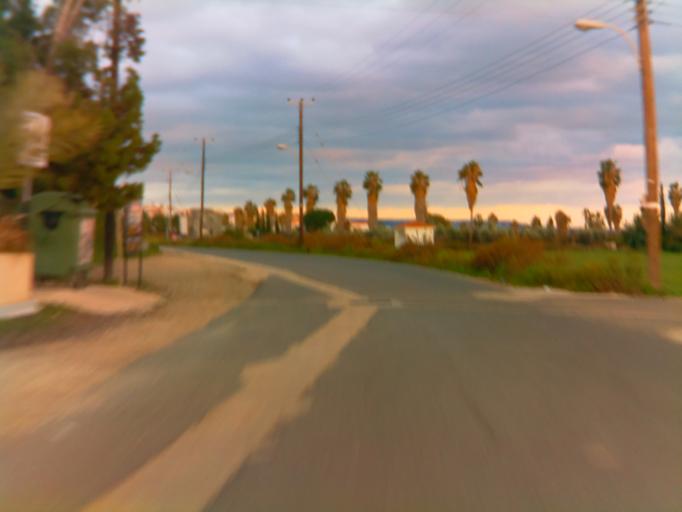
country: CY
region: Pafos
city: Pegeia
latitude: 34.8625
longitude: 32.3557
